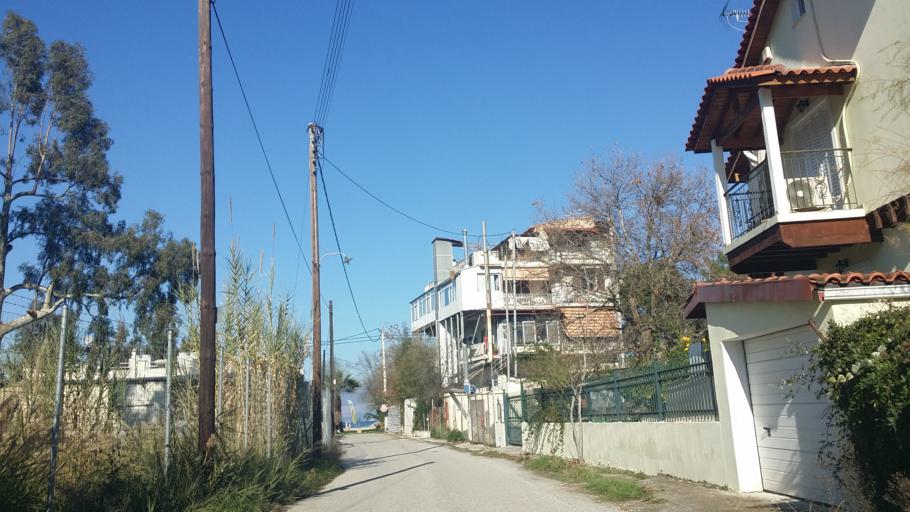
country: GR
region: West Greece
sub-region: Nomos Achaias
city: Temeni
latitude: 38.1997
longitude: 22.1800
